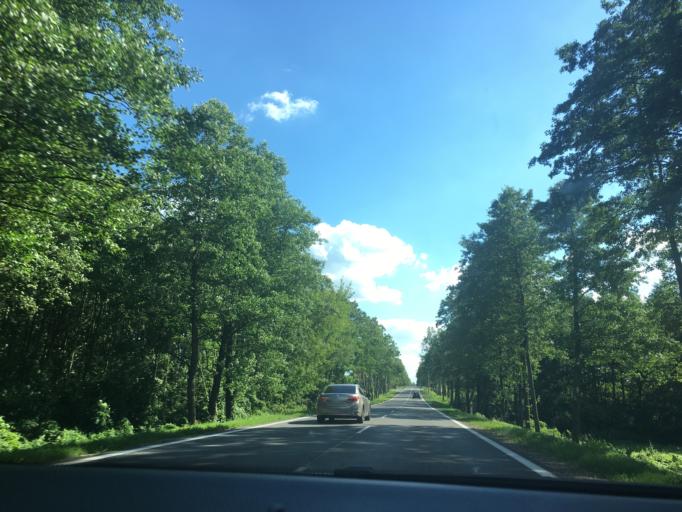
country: PL
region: Podlasie
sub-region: Powiat sokolski
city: Janow
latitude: 53.3797
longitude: 23.1107
